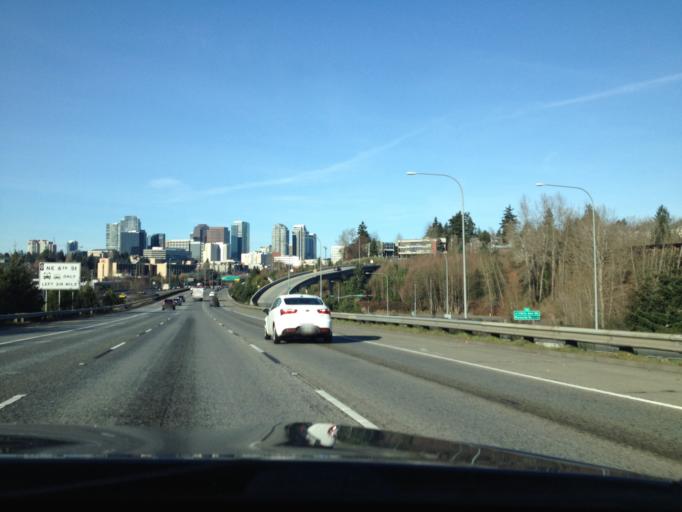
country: US
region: Washington
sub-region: King County
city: Bellevue
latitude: 47.6016
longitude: -122.1823
